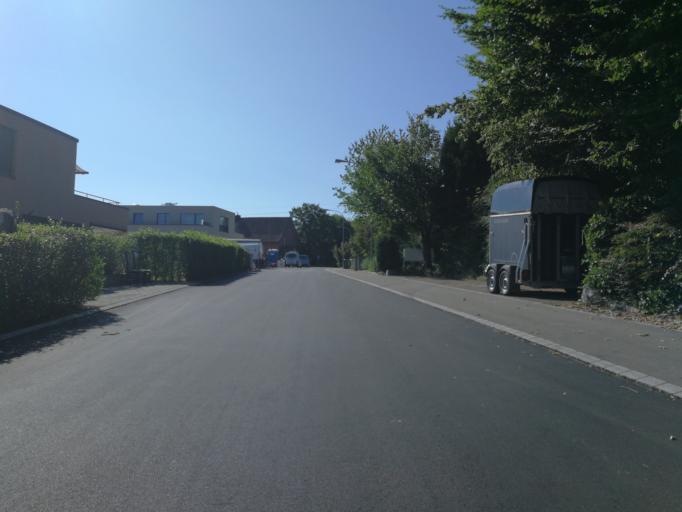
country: CH
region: Zurich
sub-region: Bezirk Uster
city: Egg
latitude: 47.2927
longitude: 8.6967
